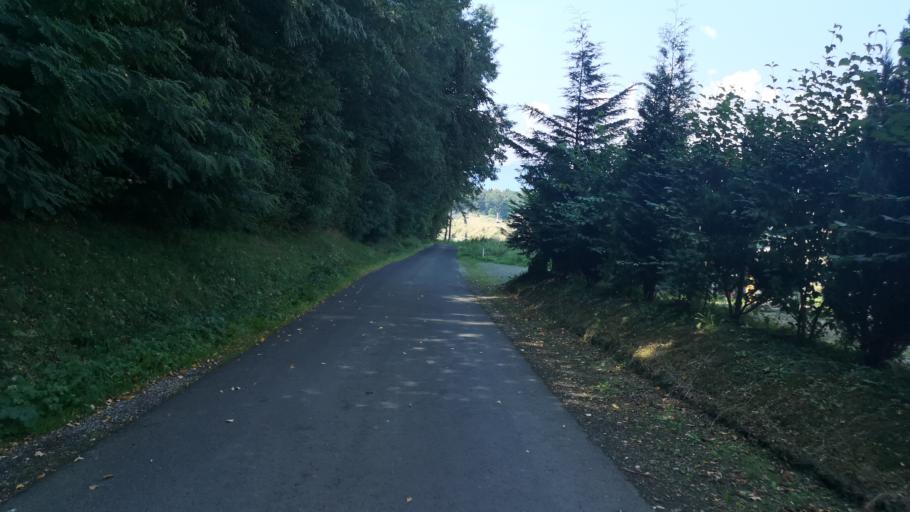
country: AT
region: Styria
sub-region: Politischer Bezirk Deutschlandsberg
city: Unterbergla
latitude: 46.8124
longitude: 15.2786
